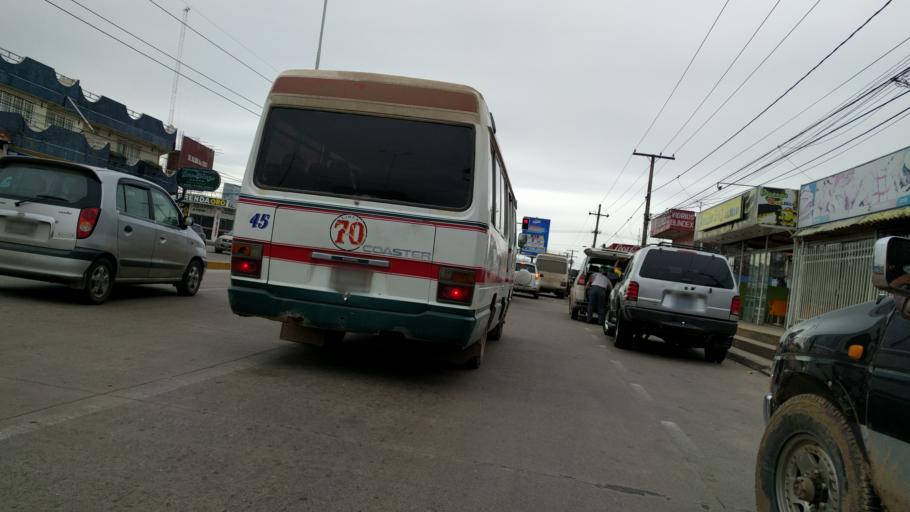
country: BO
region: Santa Cruz
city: Santa Cruz de la Sierra
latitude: -17.7786
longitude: -63.2037
